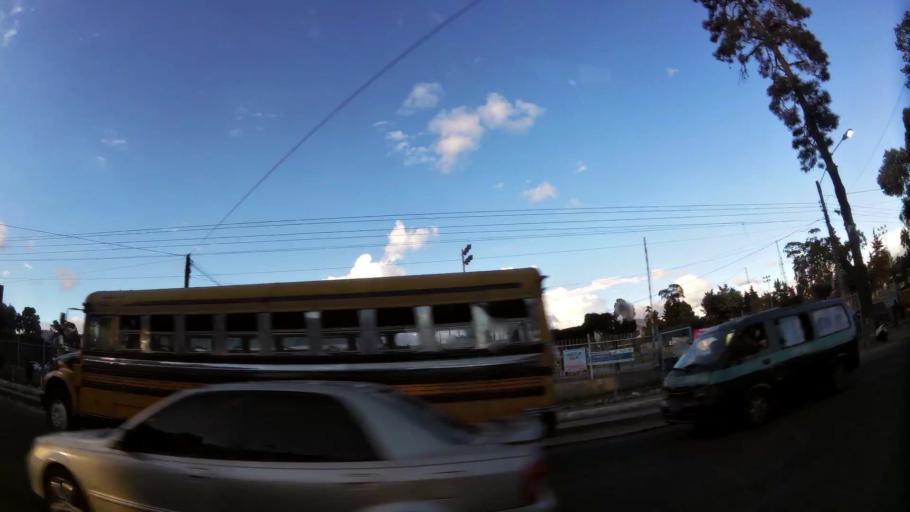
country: GT
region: Quetzaltenango
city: Quetzaltenango
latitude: 14.8457
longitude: -91.5307
